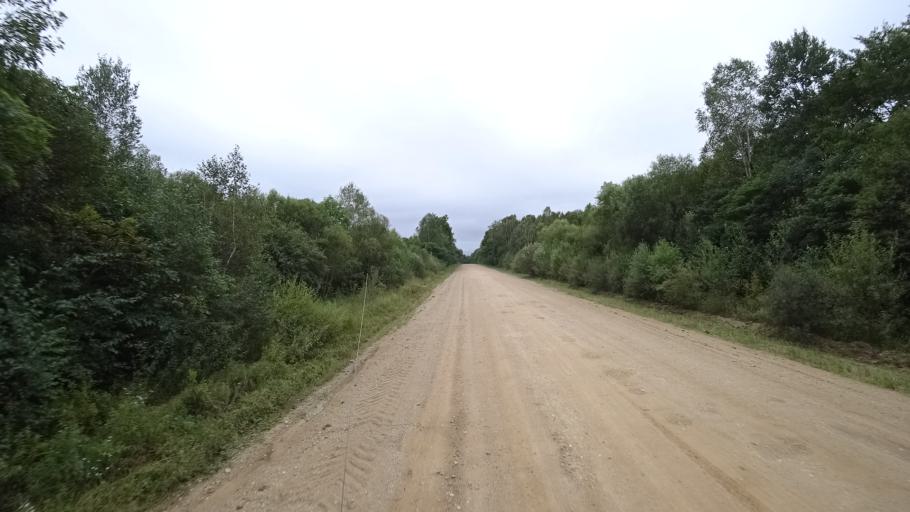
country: RU
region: Primorskiy
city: Rettikhovka
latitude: 44.1657
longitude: 132.7347
